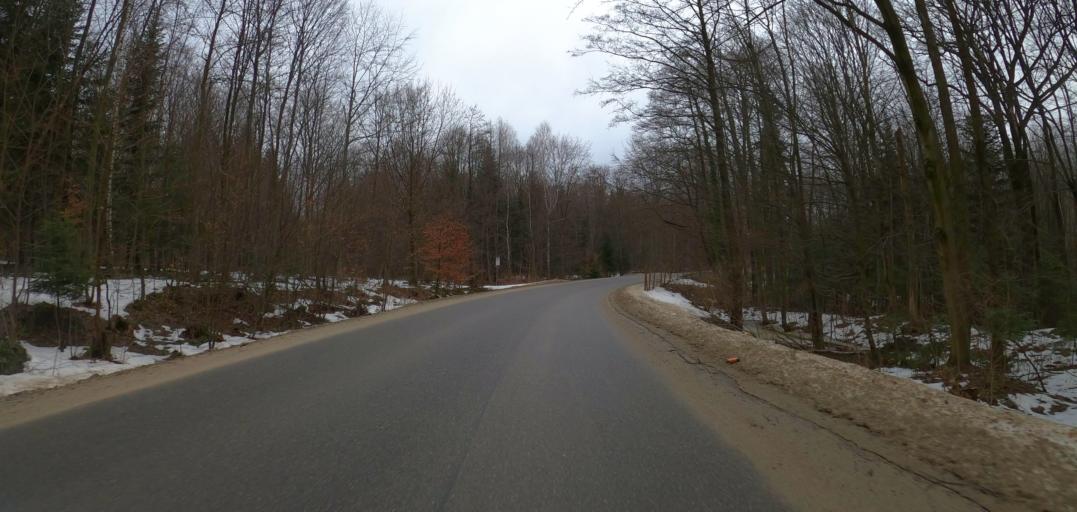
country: PL
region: Subcarpathian Voivodeship
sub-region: Powiat debicki
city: Debica
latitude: 49.9835
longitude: 21.4106
